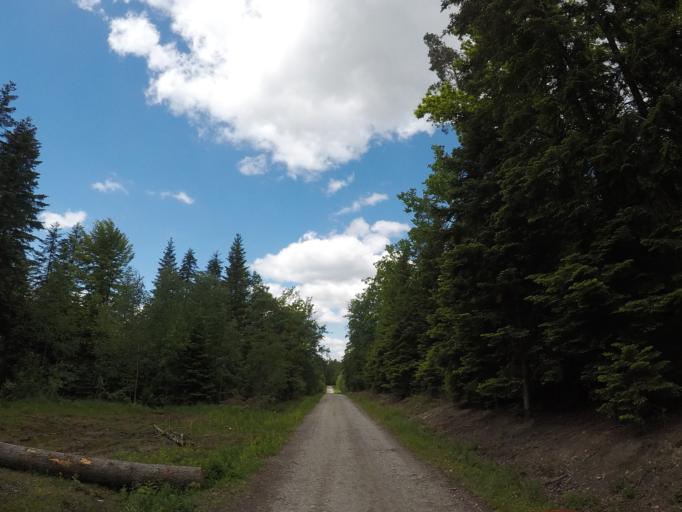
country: PL
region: Swietokrzyskie
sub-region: Powiat kielecki
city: Kielce
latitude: 50.9157
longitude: 20.6465
